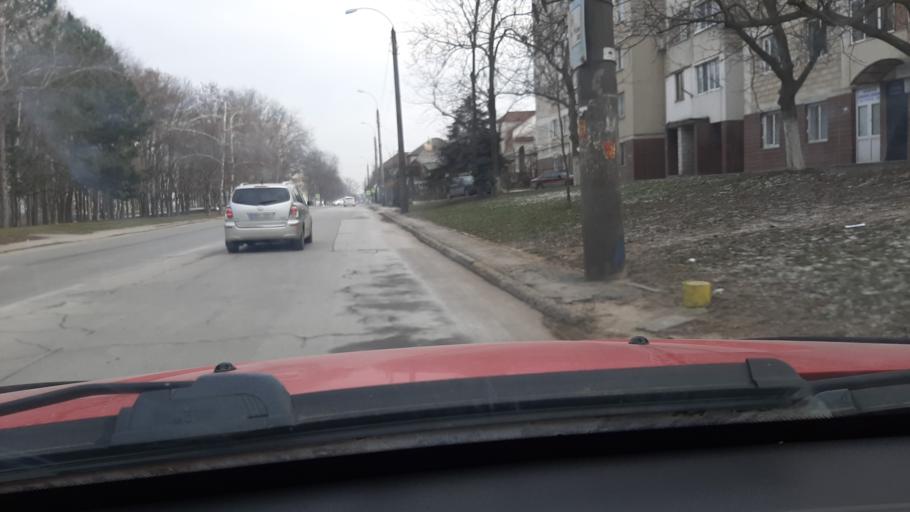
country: MD
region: Chisinau
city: Vatra
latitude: 47.0370
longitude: 28.7845
